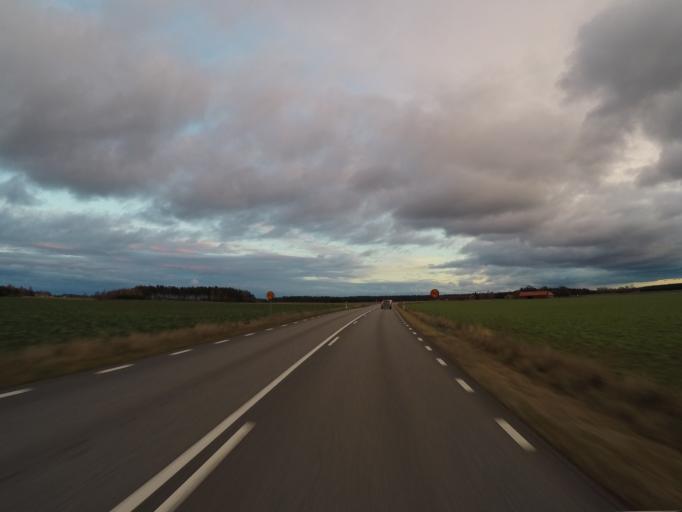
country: SE
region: Skane
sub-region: Kristianstads Kommun
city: Degeberga
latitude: 55.8949
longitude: 14.0806
